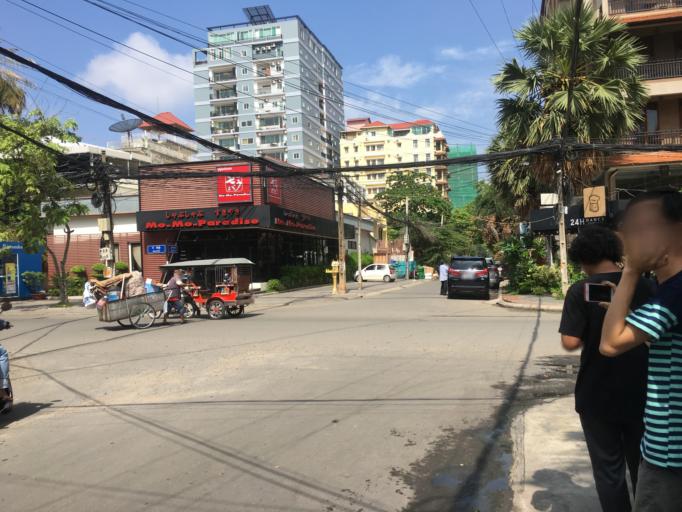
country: KH
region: Phnom Penh
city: Phnom Penh
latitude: 11.5525
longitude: 104.9267
